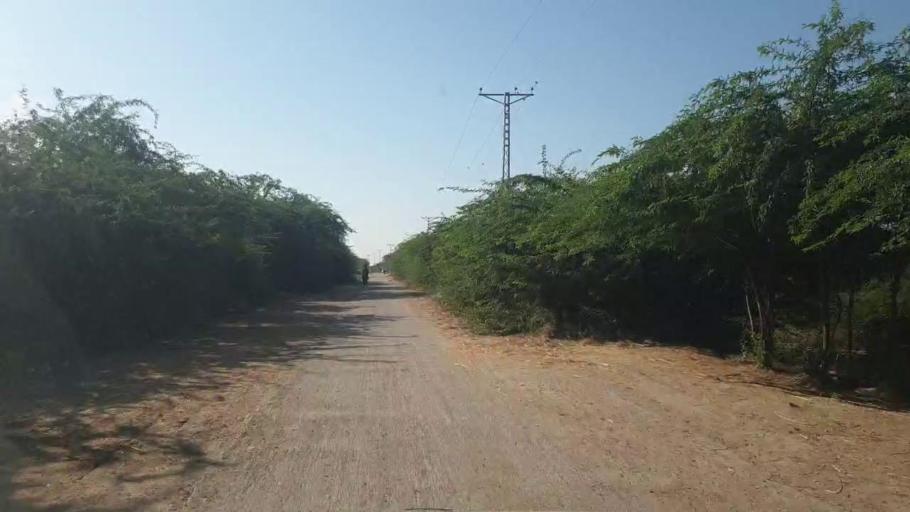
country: PK
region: Sindh
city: Talhar
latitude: 24.9486
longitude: 68.7938
